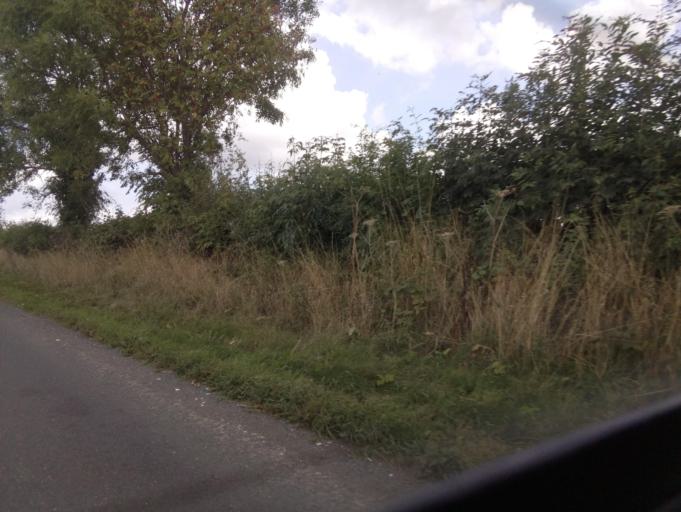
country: GB
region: England
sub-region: North Yorkshire
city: Catterick Garrison
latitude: 54.4277
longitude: -1.6819
